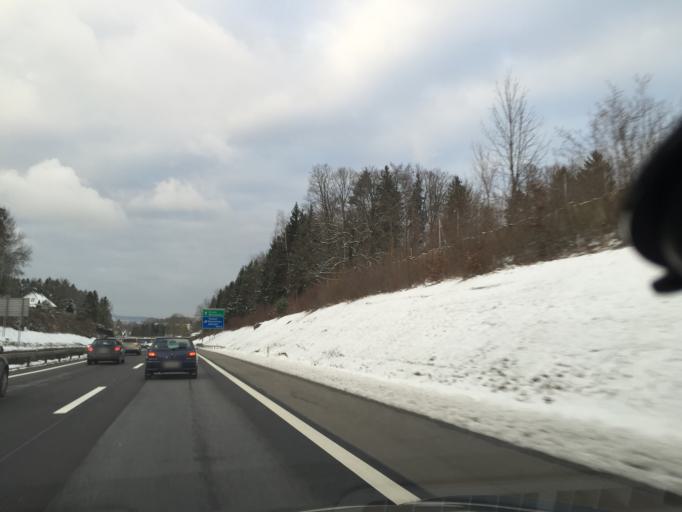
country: CH
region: Zurich
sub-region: Bezirk Horgen
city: Thalwil / Berg
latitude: 47.2944
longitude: 8.5498
